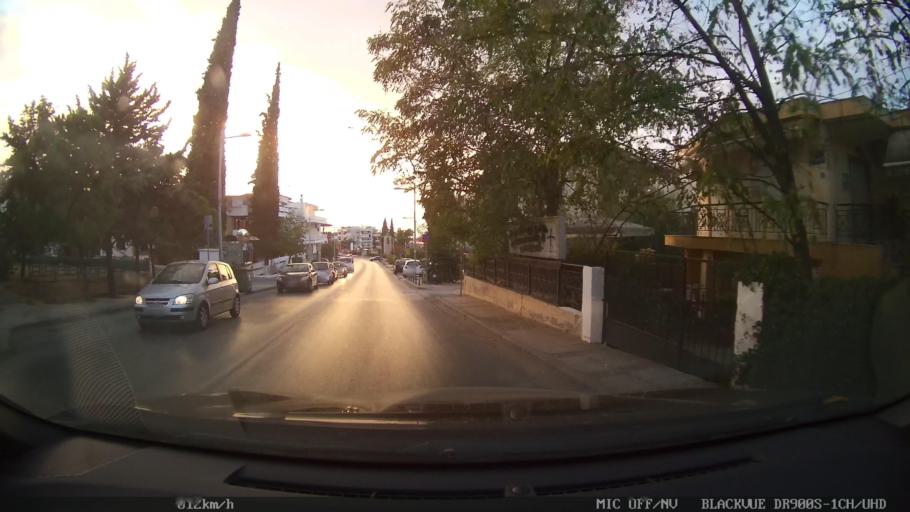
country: GR
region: Central Macedonia
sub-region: Nomos Thessalonikis
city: Pylaia
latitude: 40.6010
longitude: 22.9925
